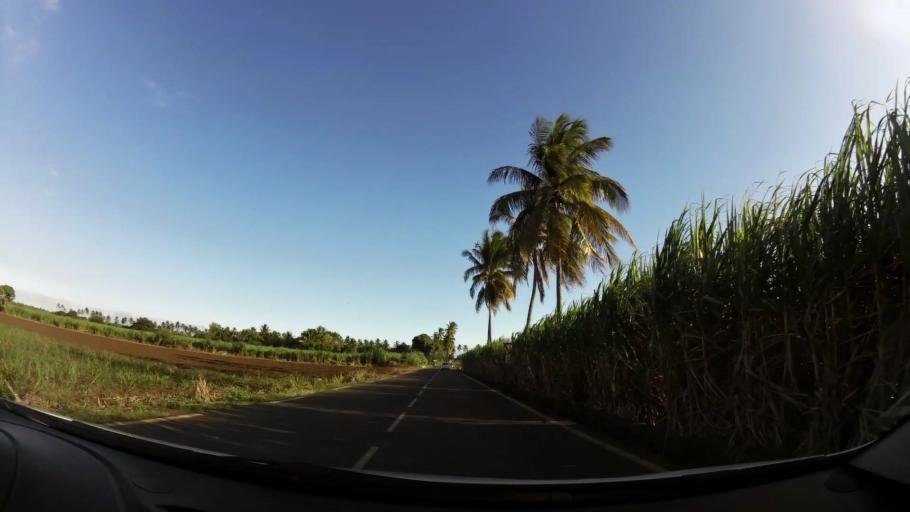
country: RE
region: Reunion
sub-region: Reunion
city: Saint-Louis
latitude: -21.2682
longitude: 55.3786
